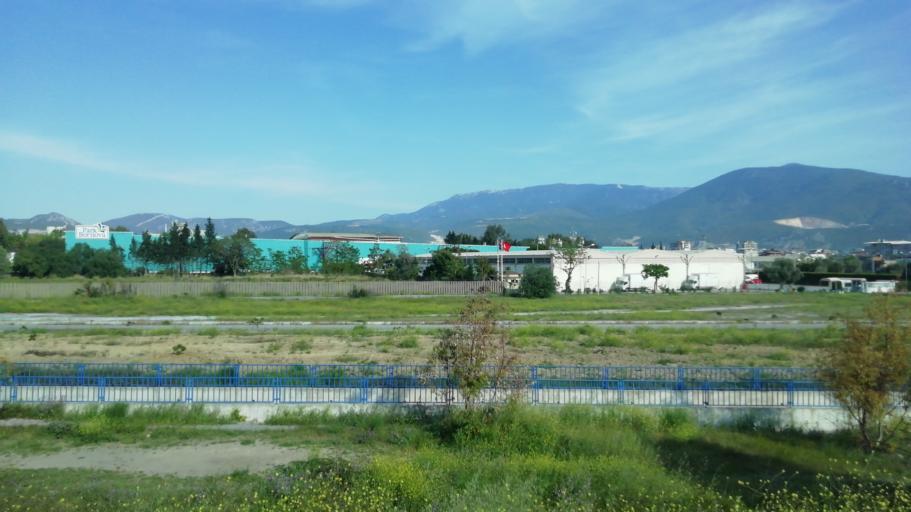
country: TR
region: Izmir
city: Bornova
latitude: 38.4575
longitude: 27.2441
